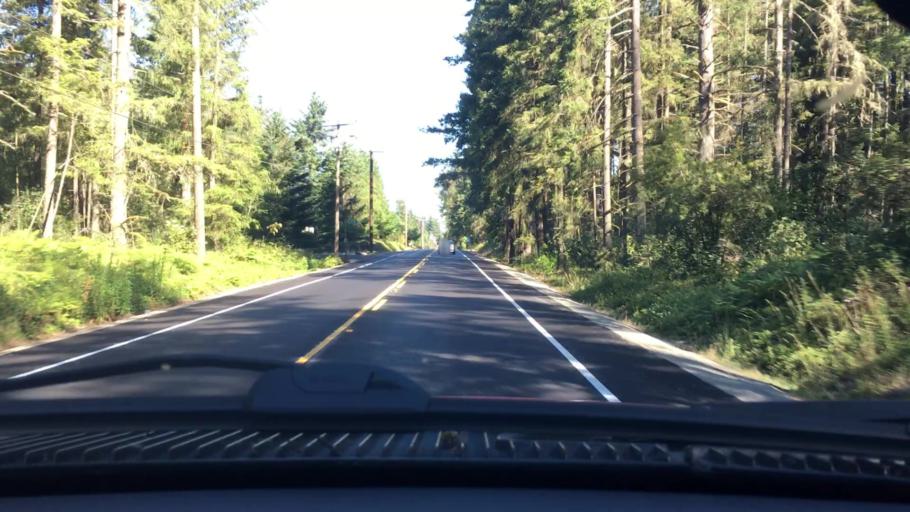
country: US
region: Washington
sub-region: King County
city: Lake Morton-Berrydale
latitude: 47.3209
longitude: -122.1065
